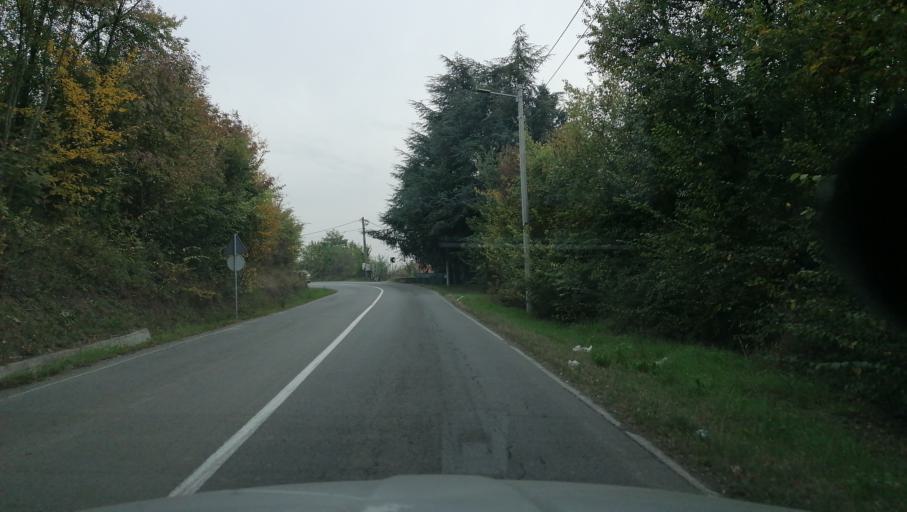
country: RS
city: Rusanj
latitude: 44.6811
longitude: 20.5042
